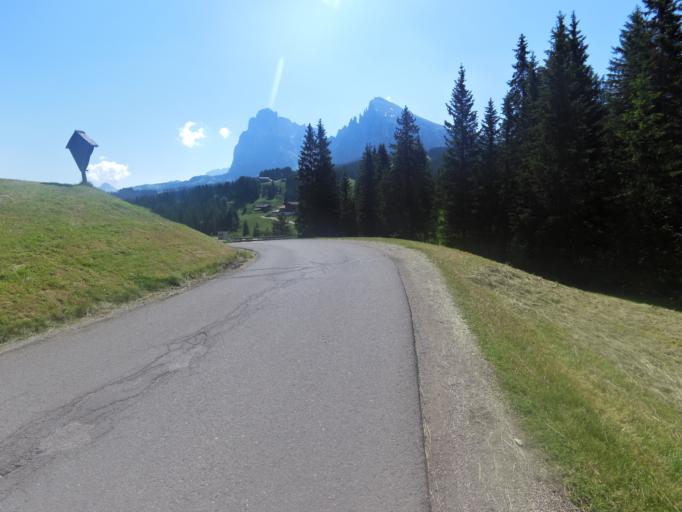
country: IT
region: Trentino-Alto Adige
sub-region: Bolzano
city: Ortisei
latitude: 46.5317
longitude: 11.6676
